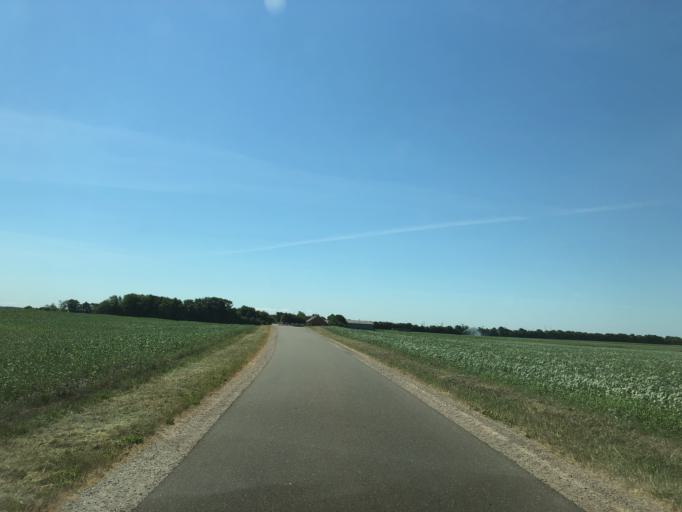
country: DK
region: Central Jutland
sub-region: Struer Kommune
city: Struer
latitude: 56.4161
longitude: 8.4256
